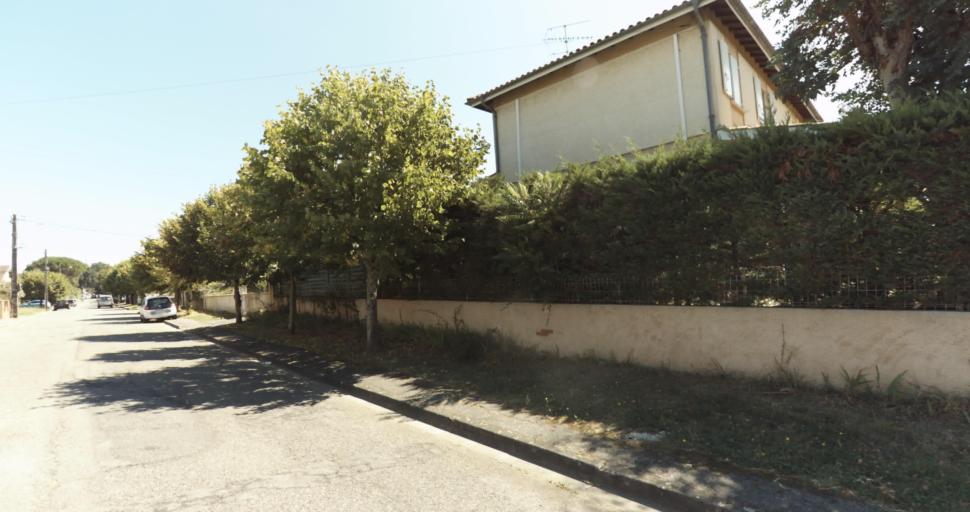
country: FR
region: Midi-Pyrenees
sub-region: Departement de la Haute-Garonne
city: L'Union
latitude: 43.6516
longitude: 1.4837
